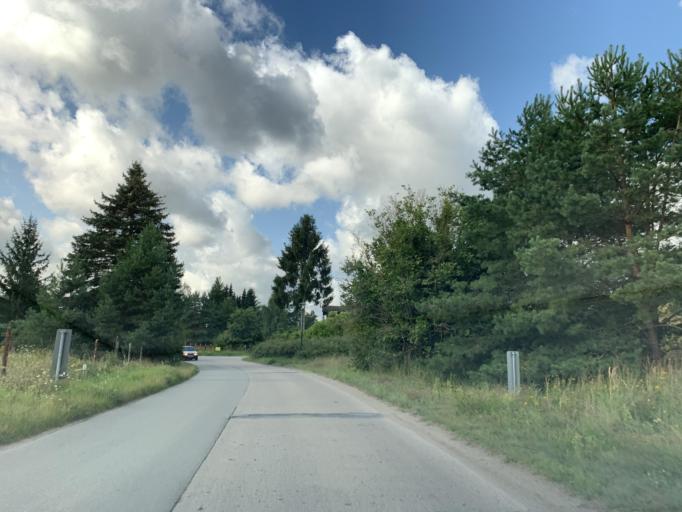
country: DE
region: Mecklenburg-Vorpommern
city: Carpin
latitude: 53.3798
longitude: 13.1839
